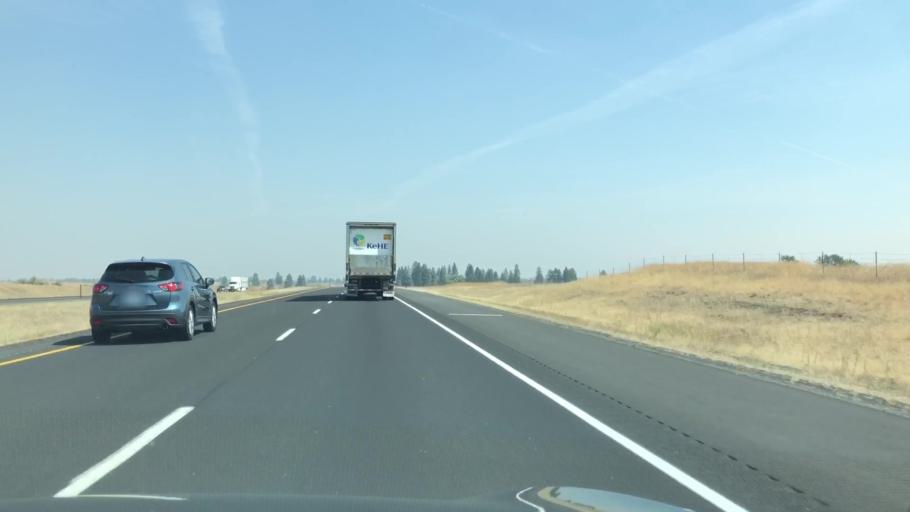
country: US
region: Washington
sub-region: Spokane County
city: Medical Lake
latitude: 47.3855
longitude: -117.8560
